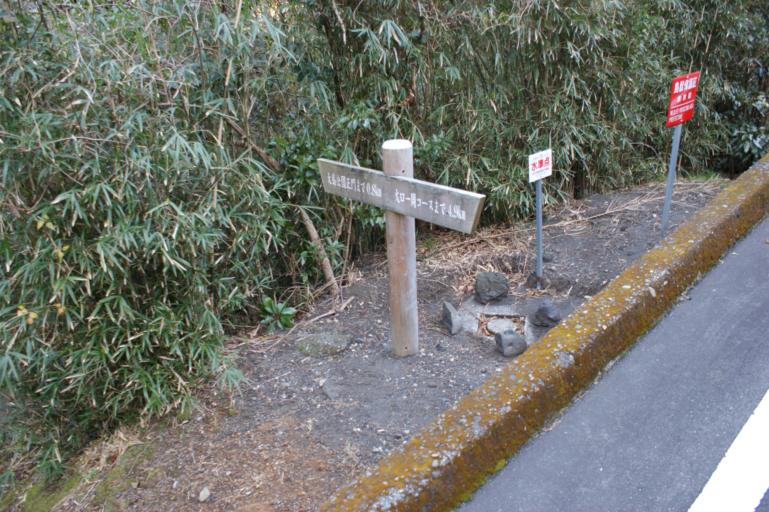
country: JP
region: Shizuoka
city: Ito
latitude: 34.7538
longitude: 139.4301
